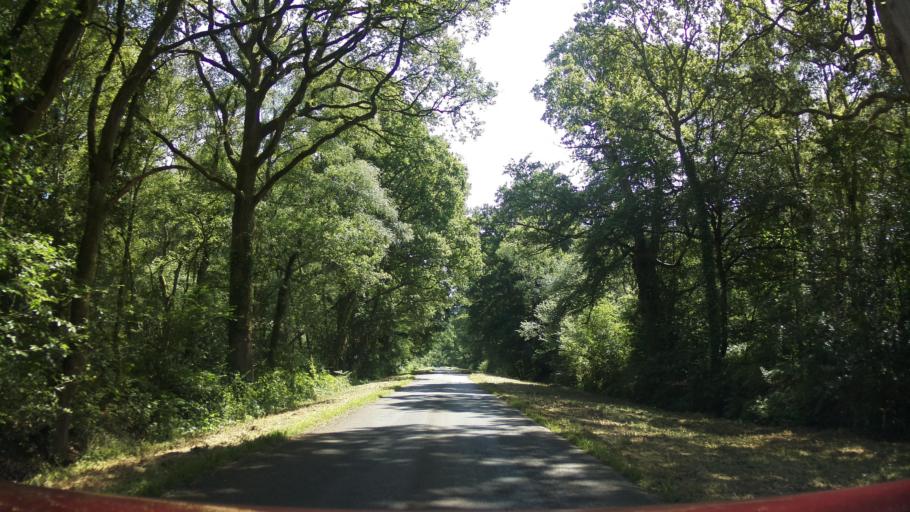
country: GB
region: England
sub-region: Wiltshire
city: Hankerton
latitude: 51.6214
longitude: -2.0114
